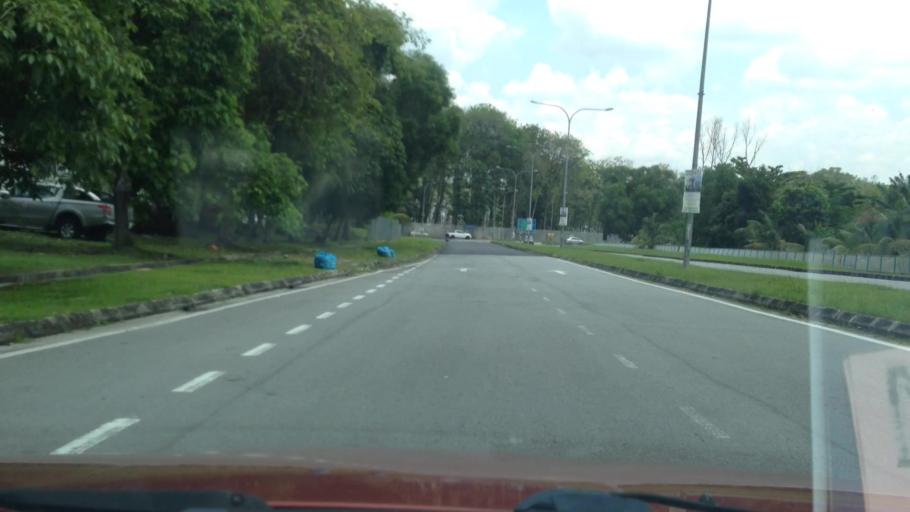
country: MY
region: Selangor
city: Kampung Baru Subang
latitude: 3.1657
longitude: 101.5501
